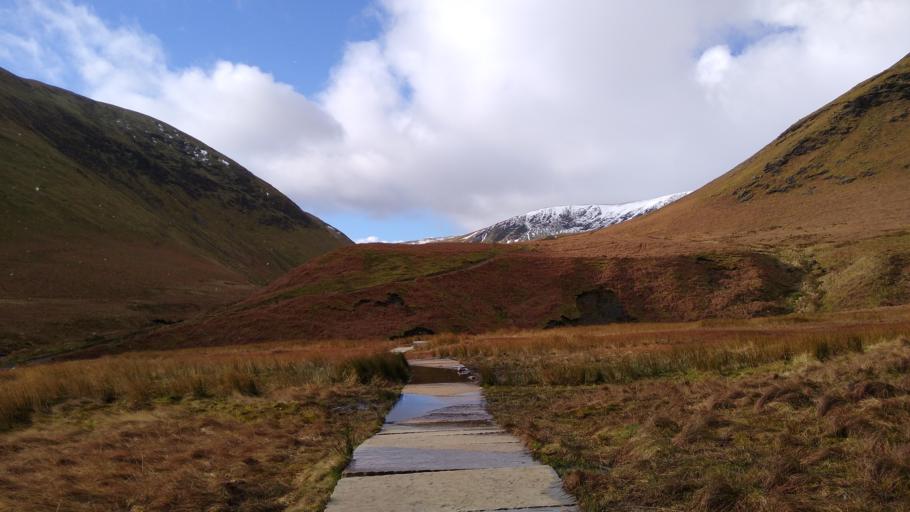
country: GB
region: England
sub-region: Cumbria
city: Keswick
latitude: 54.6639
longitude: -2.9992
